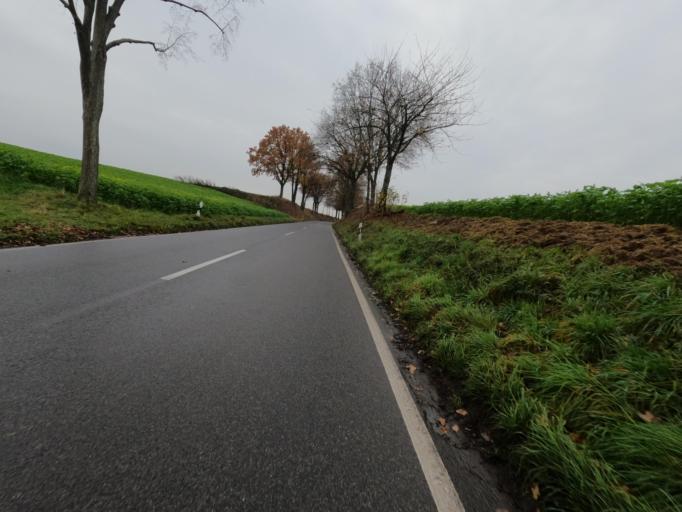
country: DE
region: North Rhine-Westphalia
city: Huckelhoven
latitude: 51.0253
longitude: 6.1732
